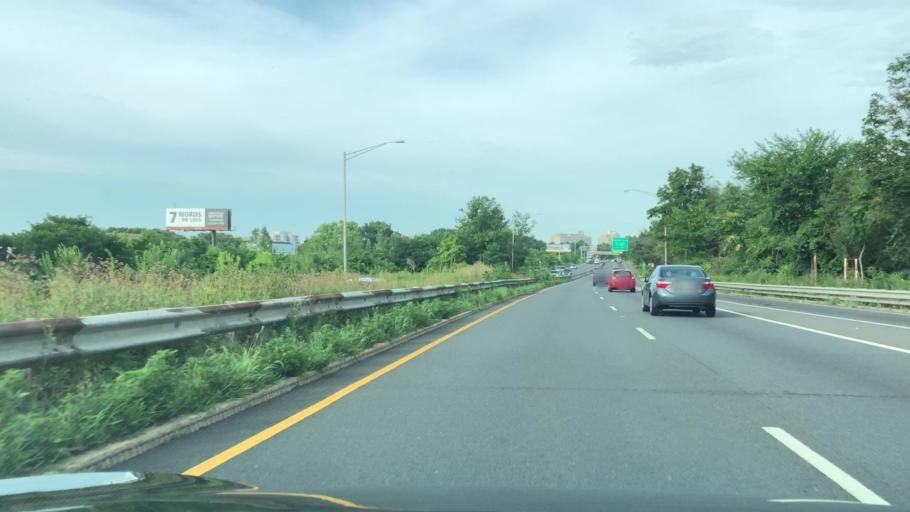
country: US
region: New Jersey
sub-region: Mercer County
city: Trenton
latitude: 40.2330
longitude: -74.7502
